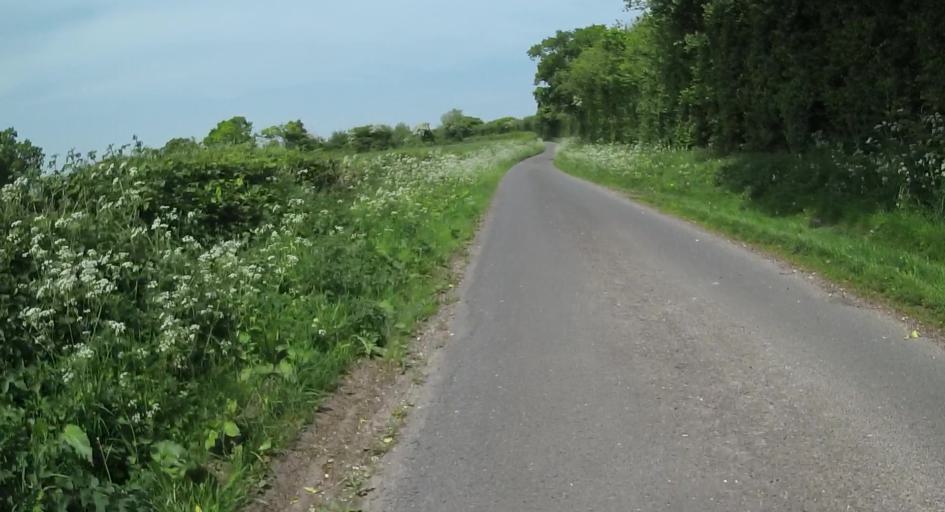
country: GB
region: England
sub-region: Hampshire
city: Overton
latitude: 51.2722
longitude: -1.2328
